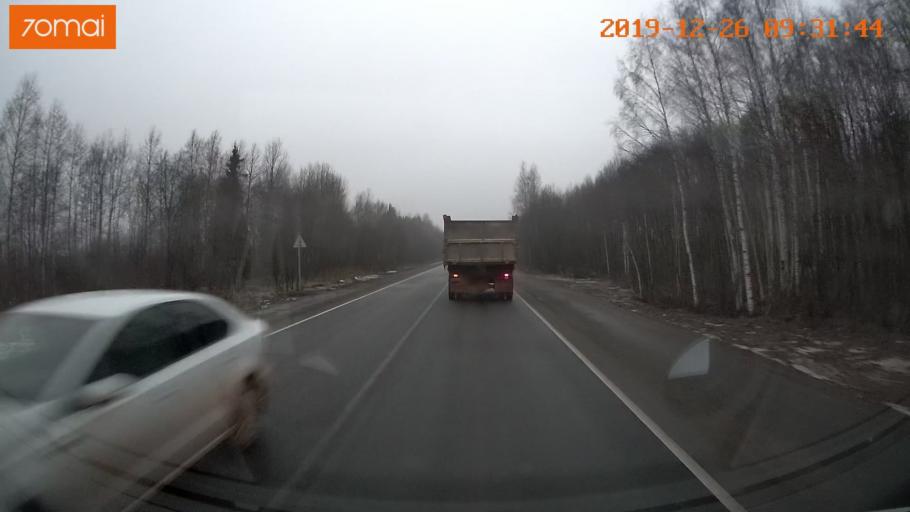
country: RU
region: Vologda
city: Gryazovets
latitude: 59.0716
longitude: 40.1247
